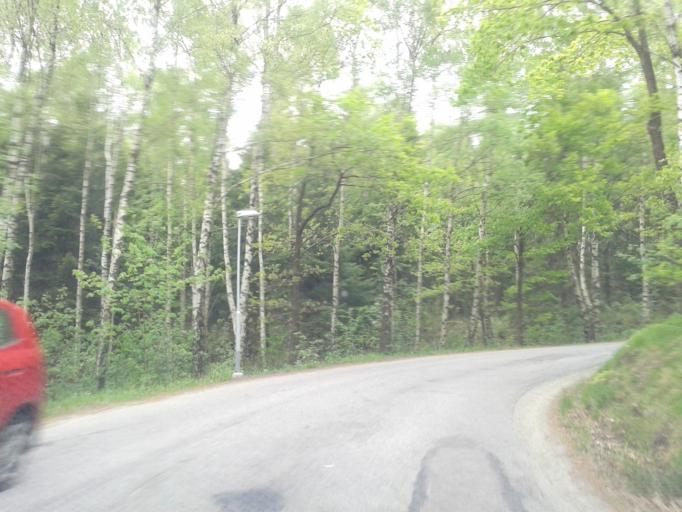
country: SE
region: Vaestra Goetaland
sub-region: Kungalvs Kommun
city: Kungalv
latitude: 57.8734
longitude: 11.9924
